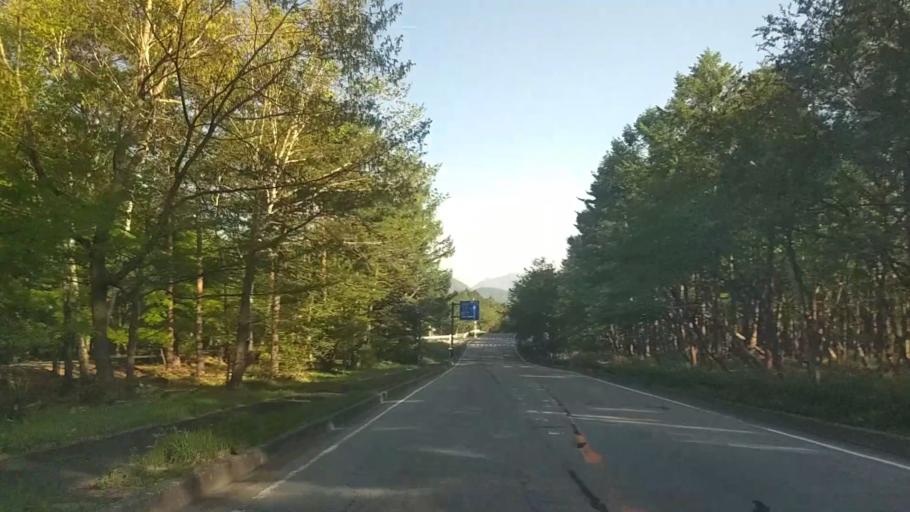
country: JP
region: Yamanashi
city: Nirasaki
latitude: 35.9238
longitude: 138.4330
